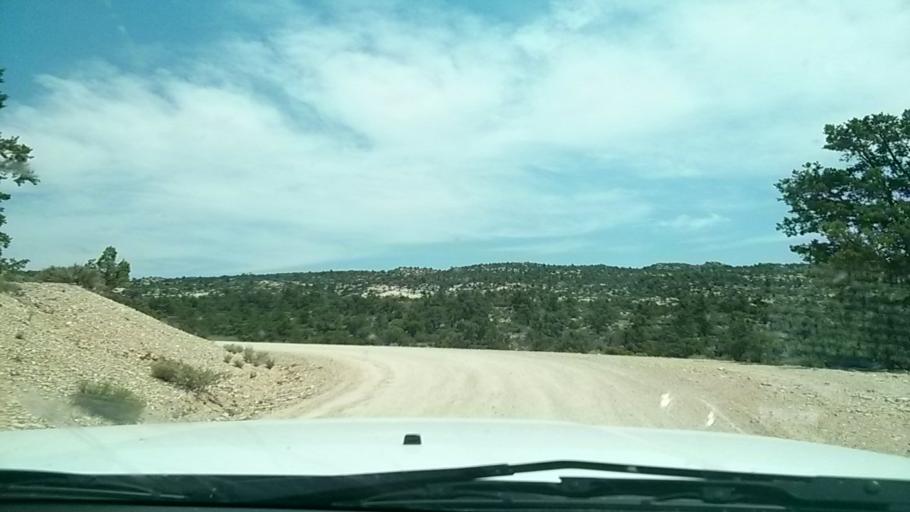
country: US
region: Utah
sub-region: Washington County
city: Toquerville
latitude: 37.2665
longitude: -113.4115
